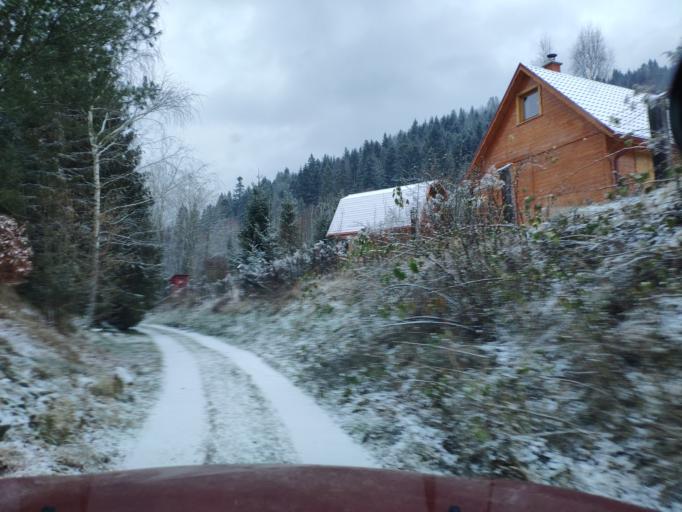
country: SK
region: Kosicky
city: Spisska Nova Ves
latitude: 48.8170
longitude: 20.5492
